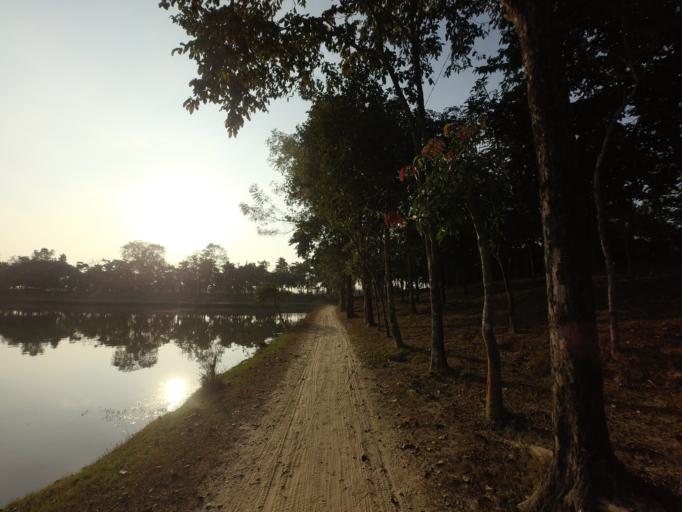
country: BD
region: Rajshahi
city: Saidpur
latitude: 26.0054
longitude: 88.7543
